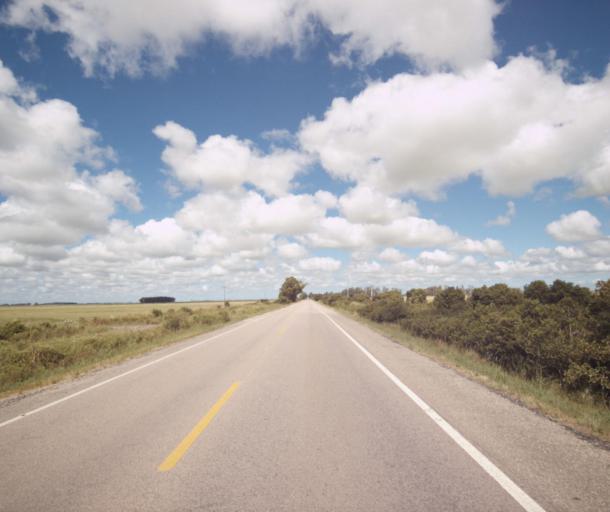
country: BR
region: Rio Grande do Sul
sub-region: Rio Grande
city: Rio Grande
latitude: -32.1765
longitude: -52.4187
